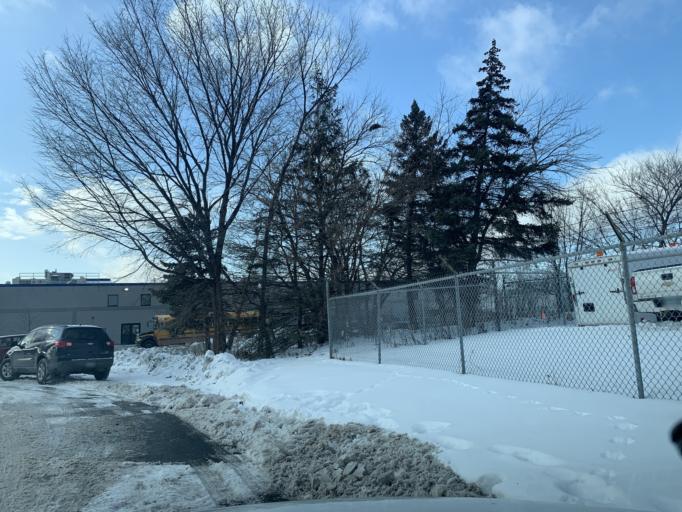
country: US
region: Minnesota
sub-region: Hennepin County
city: Minneapolis
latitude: 44.9909
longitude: -93.2907
